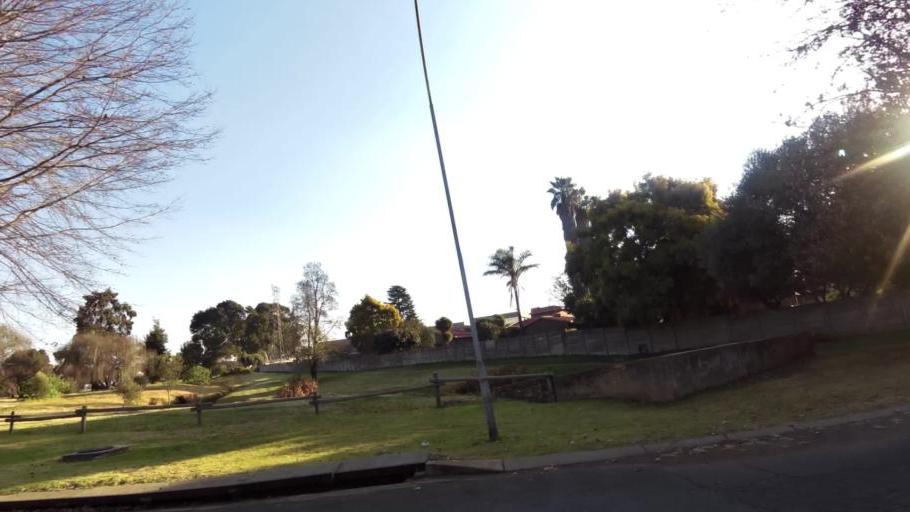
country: ZA
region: Gauteng
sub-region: City of Johannesburg Metropolitan Municipality
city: Johannesburg
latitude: -26.1594
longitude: 27.9803
